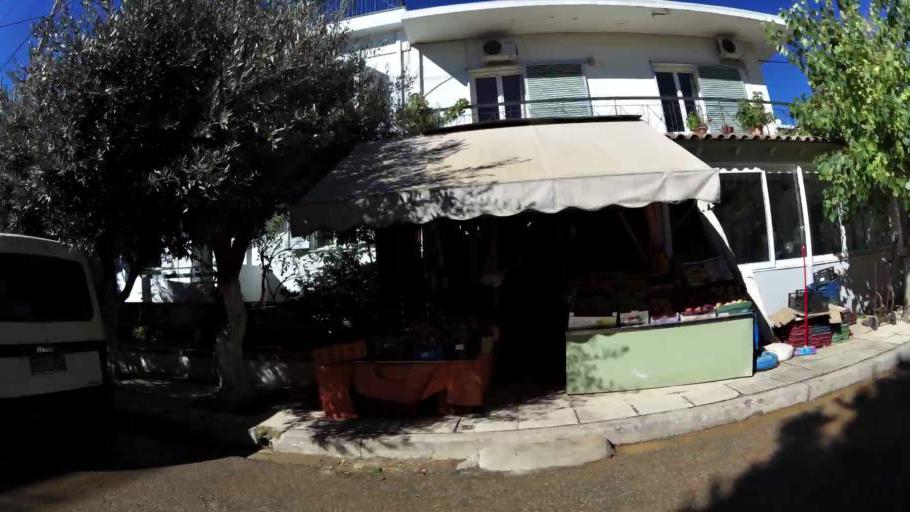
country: GR
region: Attica
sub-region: Nomarchia Athinas
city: Vrilissia
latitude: 38.0327
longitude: 23.8146
